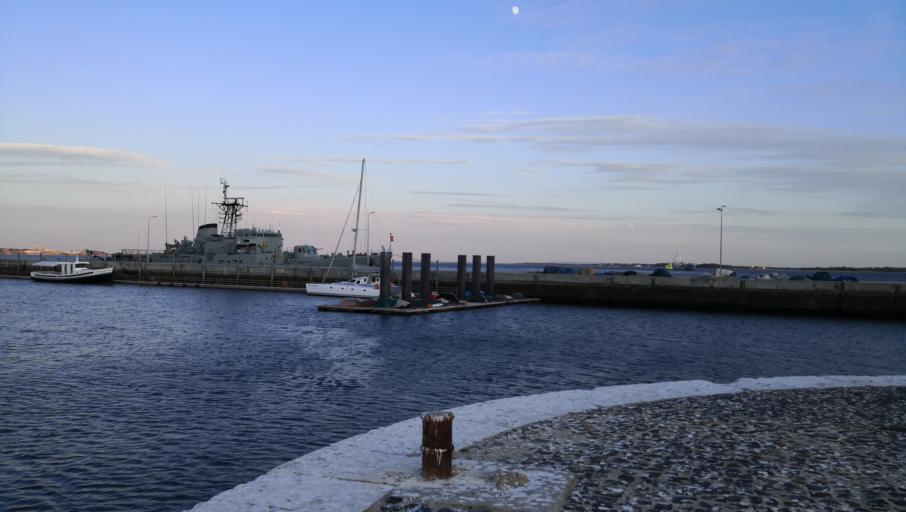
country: PT
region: Setubal
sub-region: Setubal
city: Setubal
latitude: 38.5191
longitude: -8.8998
